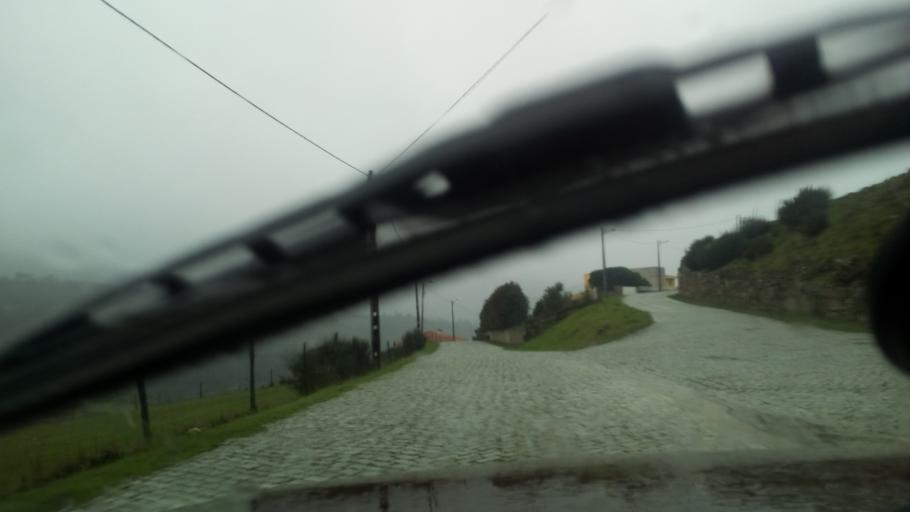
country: PT
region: Guarda
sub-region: Celorico da Beira
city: Celorico da Beira
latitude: 40.5400
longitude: -7.4578
